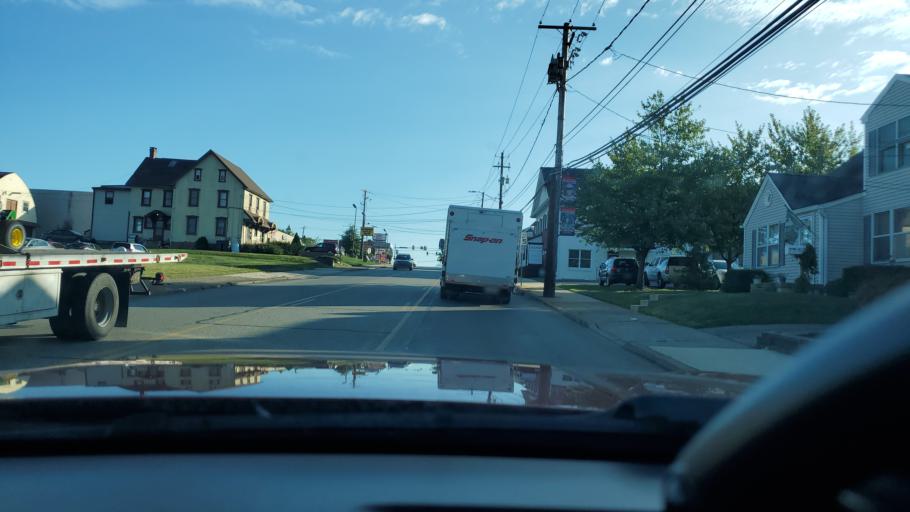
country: US
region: Pennsylvania
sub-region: Montgomery County
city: Souderton
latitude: 40.3134
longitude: -75.3131
